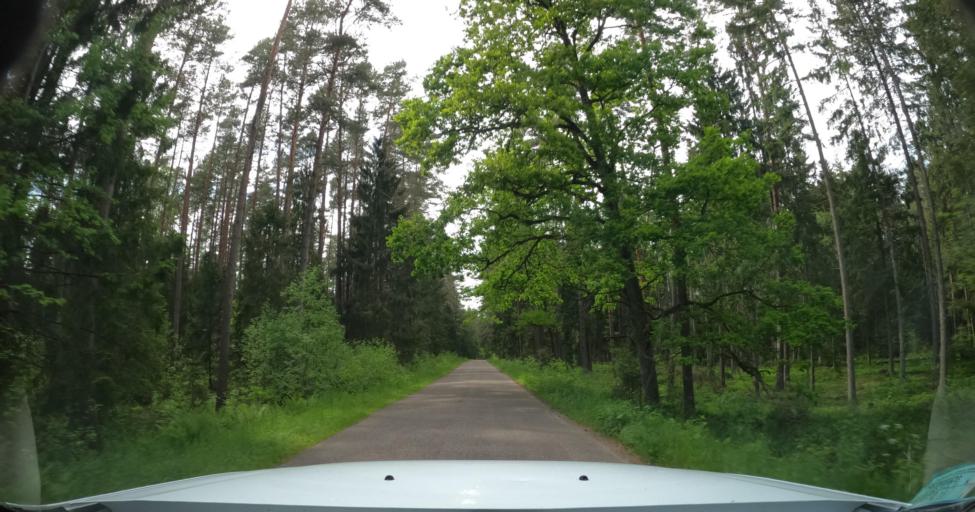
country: PL
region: Warmian-Masurian Voivodeship
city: Dobre Miasto
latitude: 54.0976
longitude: 20.3854
